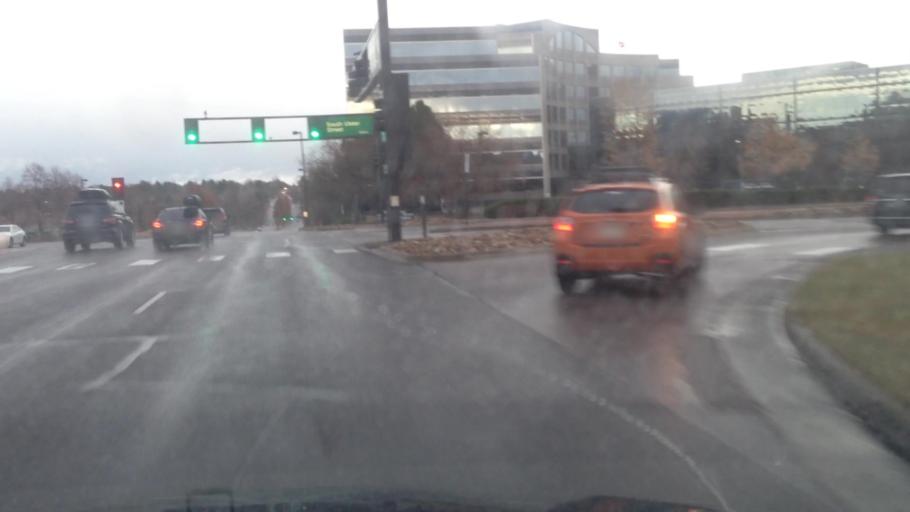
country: US
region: Colorado
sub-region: Arapahoe County
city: Castlewood
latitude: 39.6240
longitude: -104.8951
